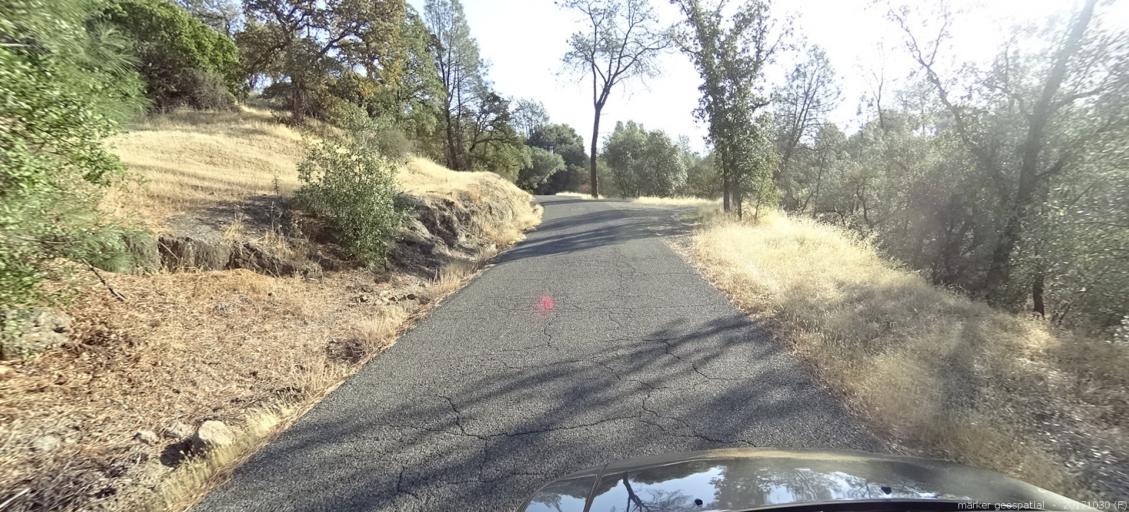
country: US
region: California
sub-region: Shasta County
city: Palo Cedro
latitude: 40.5676
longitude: -122.1403
